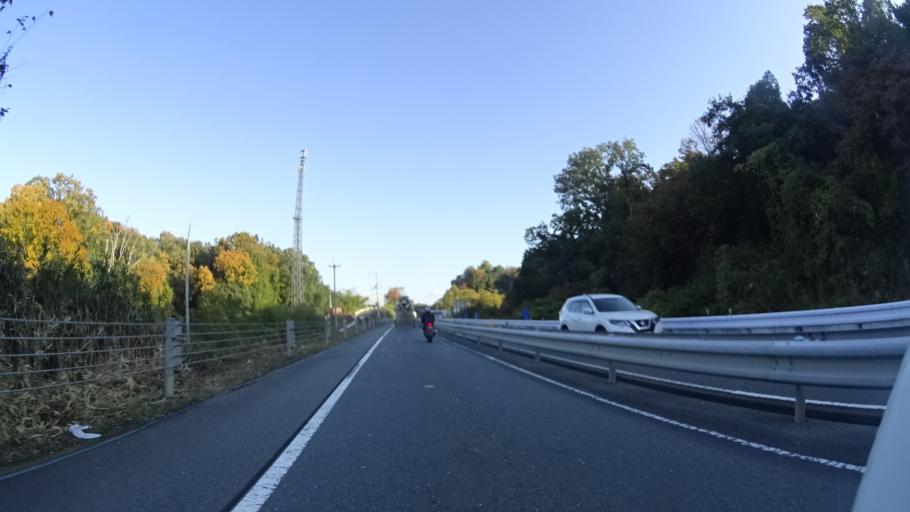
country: JP
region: Shiga Prefecture
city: Kitahama
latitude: 35.1225
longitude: 135.8988
